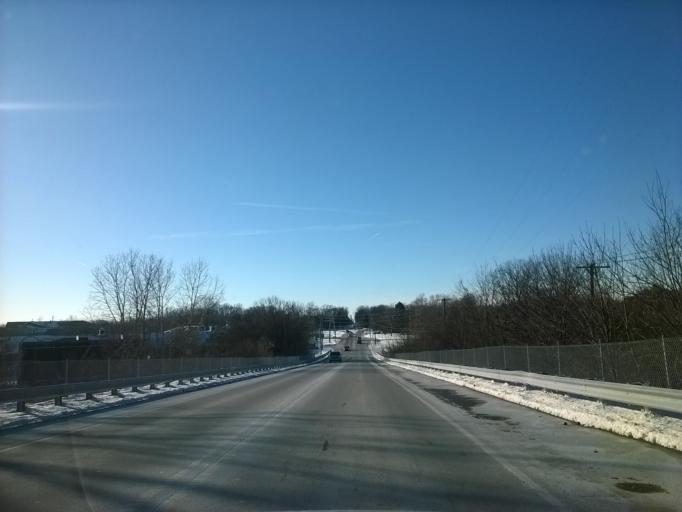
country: US
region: Indiana
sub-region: Marion County
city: Meridian Hills
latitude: 39.9269
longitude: -86.1792
